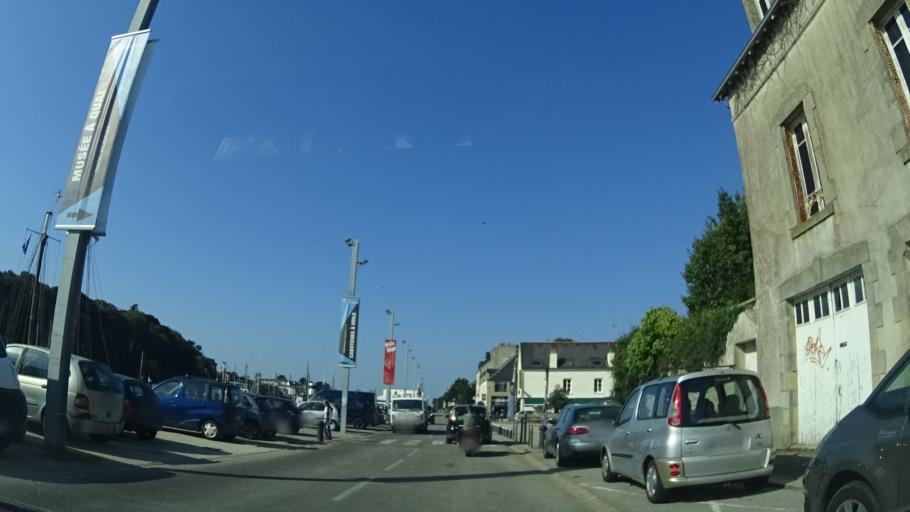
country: FR
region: Brittany
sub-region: Departement du Finistere
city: Douarnenez
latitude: 48.0921
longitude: -4.3332
